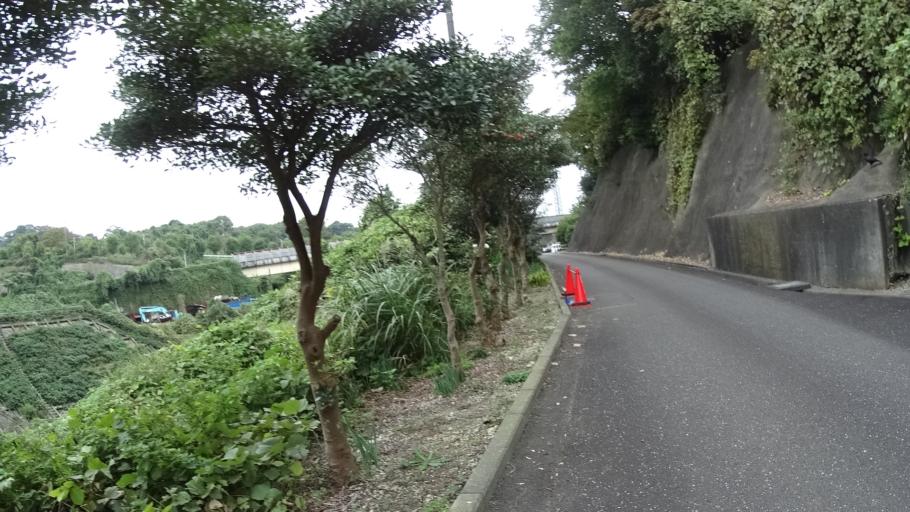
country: JP
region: Kanagawa
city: Zushi
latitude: 35.2945
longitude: 139.6198
